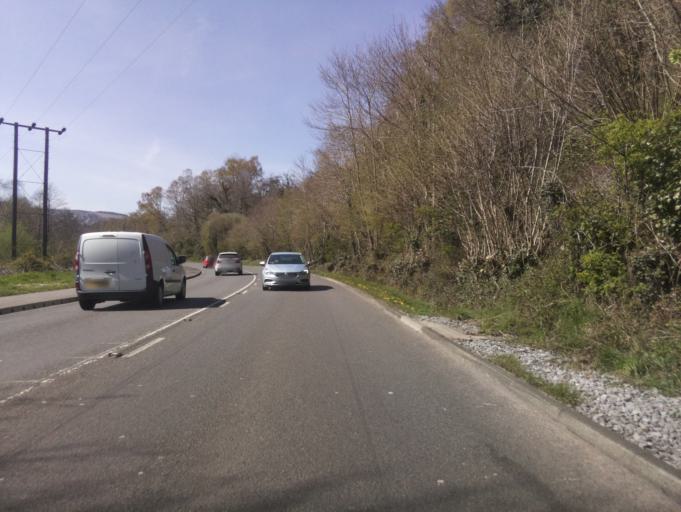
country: GB
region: Wales
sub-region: Merthyr Tydfil County Borough
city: Treharris
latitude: 51.6635
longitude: -3.3429
